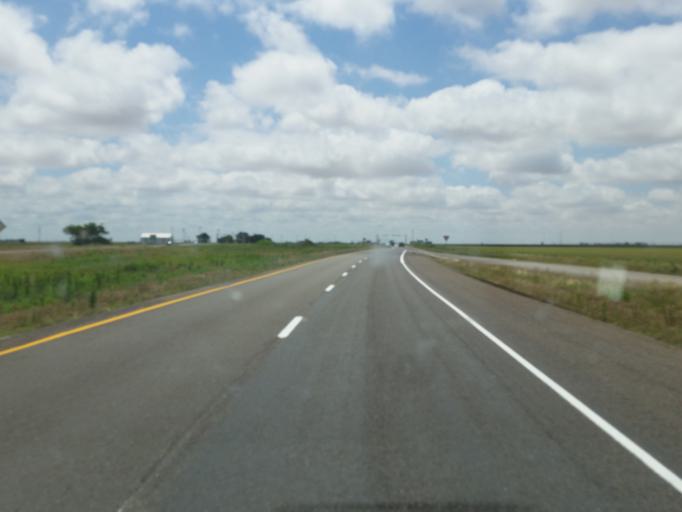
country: US
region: Texas
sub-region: Lubbock County
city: Slaton
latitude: 33.4176
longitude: -101.6389
